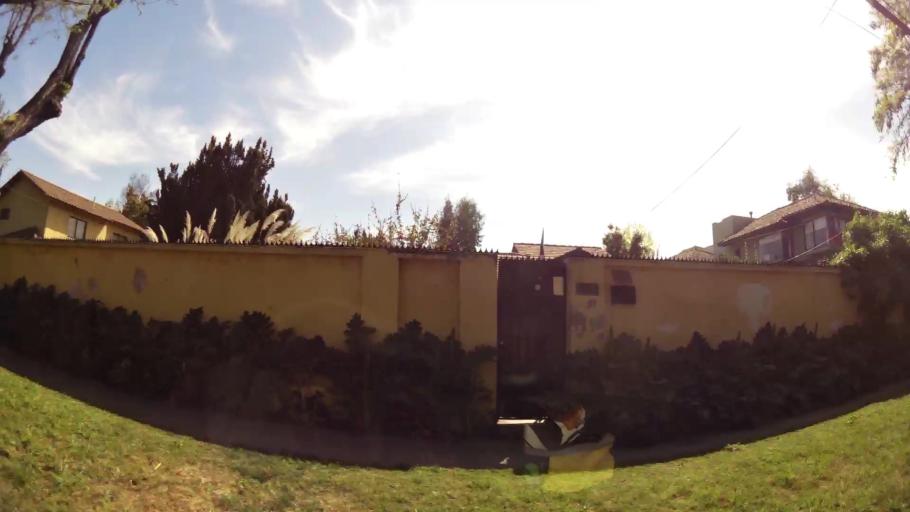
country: CL
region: Santiago Metropolitan
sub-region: Provincia de Santiago
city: Villa Presidente Frei, Nunoa, Santiago, Chile
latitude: -33.4373
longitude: -70.5492
